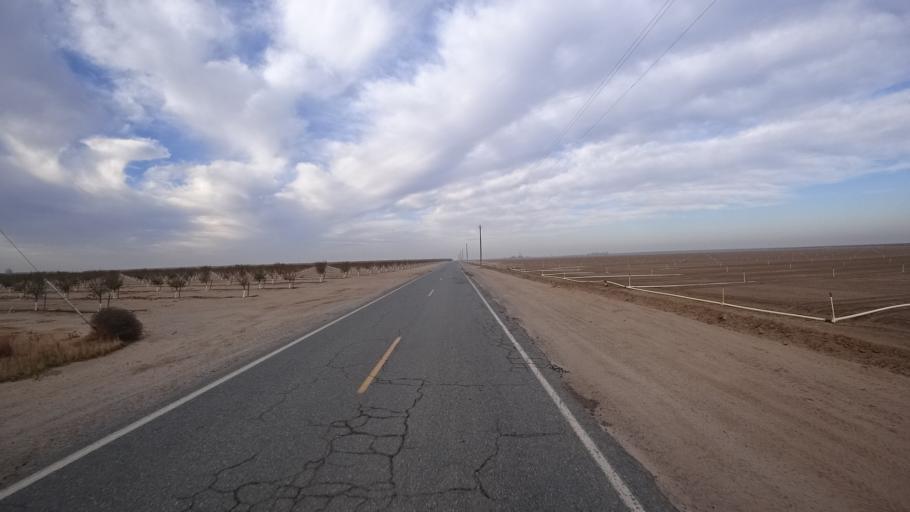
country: US
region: California
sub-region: Kern County
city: Rosedale
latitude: 35.4125
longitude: -119.1830
